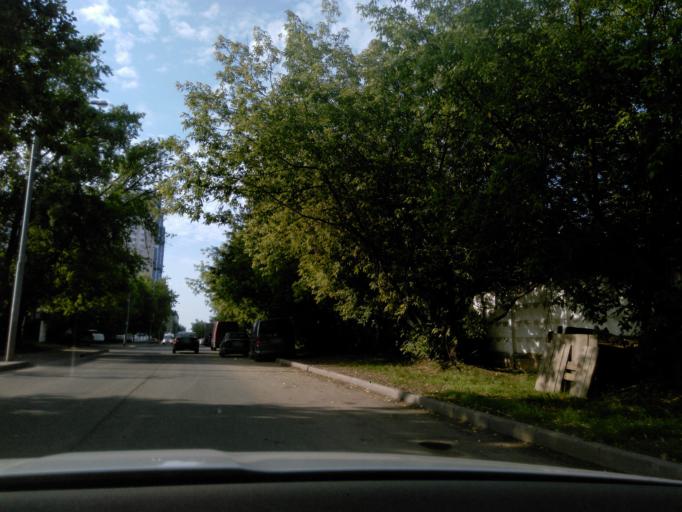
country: RU
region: Moskovskaya
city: Levoberezhnaya
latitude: 55.8734
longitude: 37.4723
